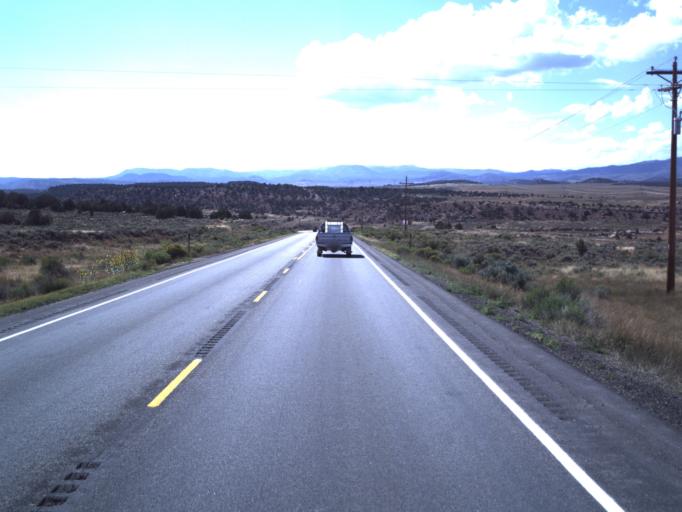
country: US
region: Utah
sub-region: Duchesne County
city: Duchesne
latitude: 40.2098
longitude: -110.7499
